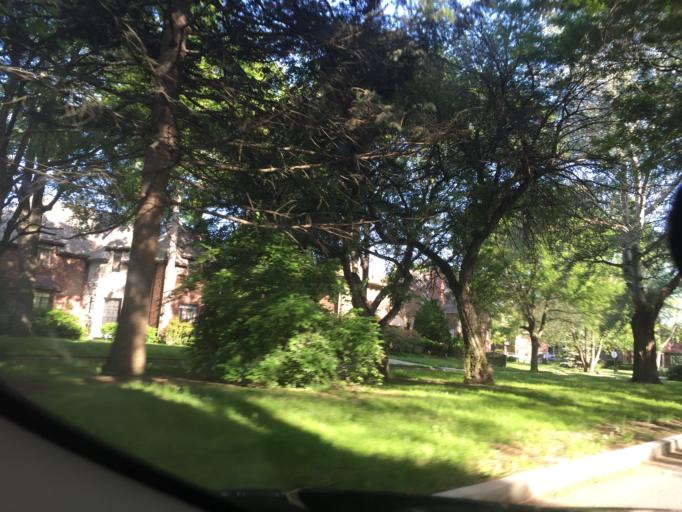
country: US
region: Michigan
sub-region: Oakland County
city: Southfield
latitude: 42.4064
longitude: -83.2284
